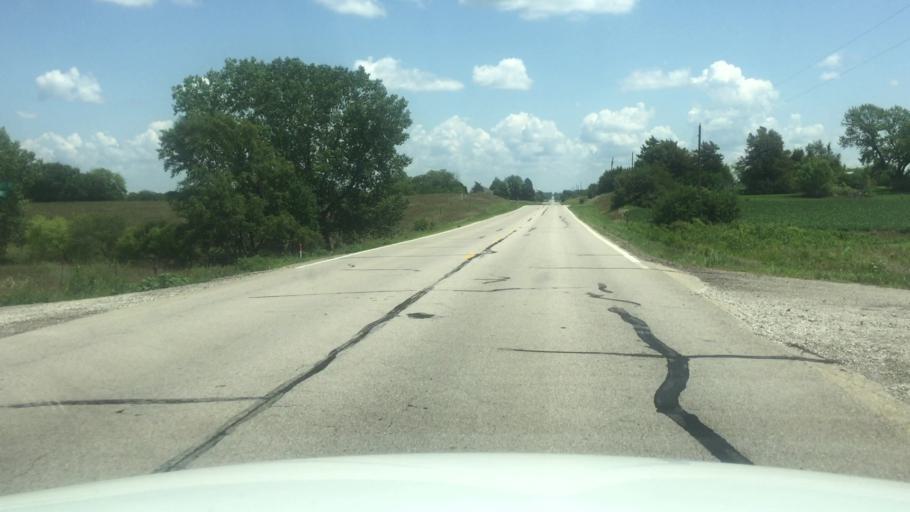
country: US
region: Kansas
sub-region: Brown County
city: Horton
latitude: 39.6674
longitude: -95.5829
